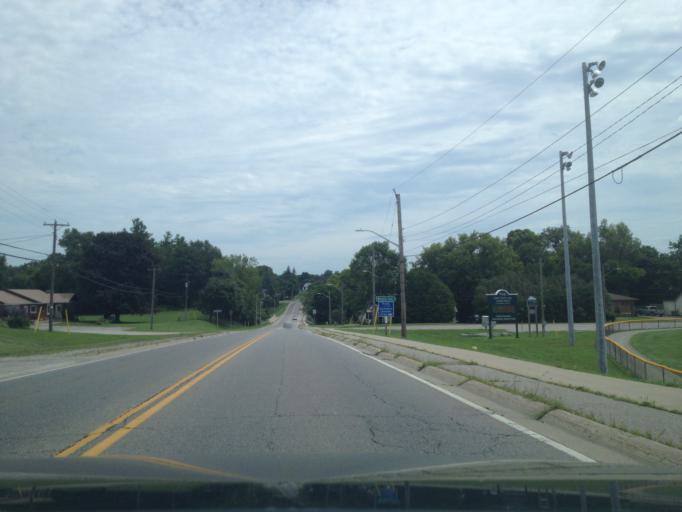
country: CA
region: Ontario
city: Norfolk County
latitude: 42.8559
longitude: -80.5064
